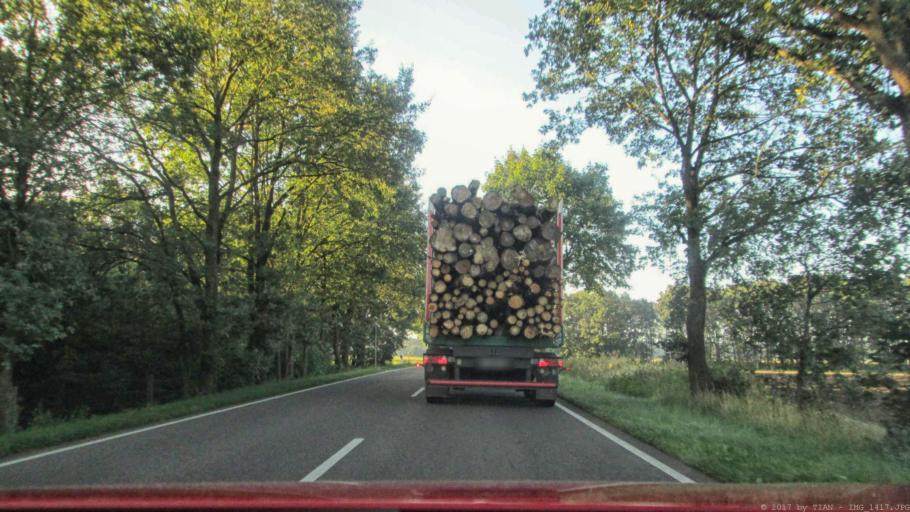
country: DE
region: Lower Saxony
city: Bodenteich
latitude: 52.7939
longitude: 10.7151
